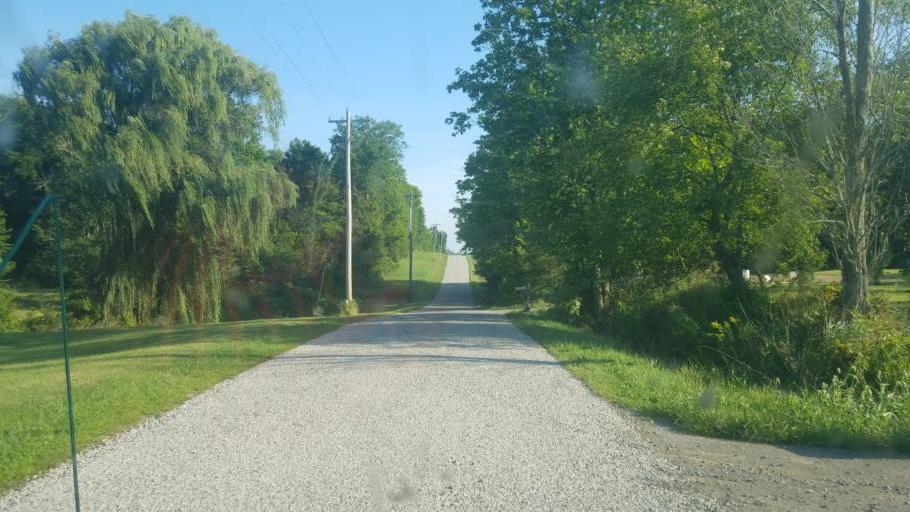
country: US
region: Ohio
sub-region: Ashland County
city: Ashland
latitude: 40.9482
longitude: -82.3398
